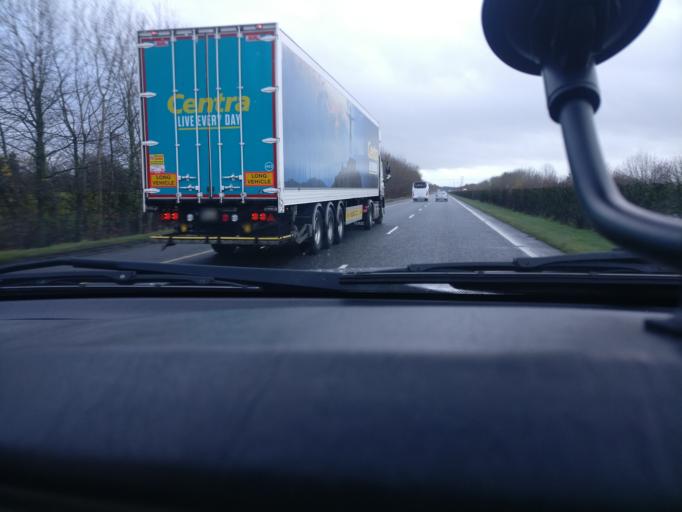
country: IE
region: Leinster
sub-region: Kildare
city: Kilcock
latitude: 53.3790
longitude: -6.6434
